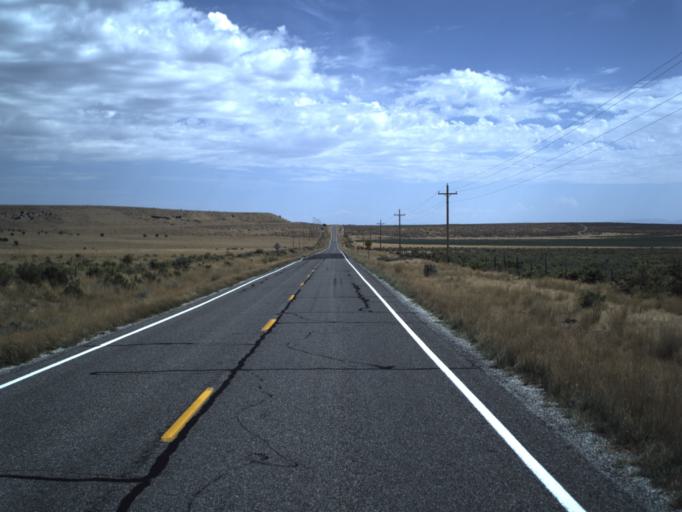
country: US
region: Idaho
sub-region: Cassia County
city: Burley
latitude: 41.8165
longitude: -113.2389
